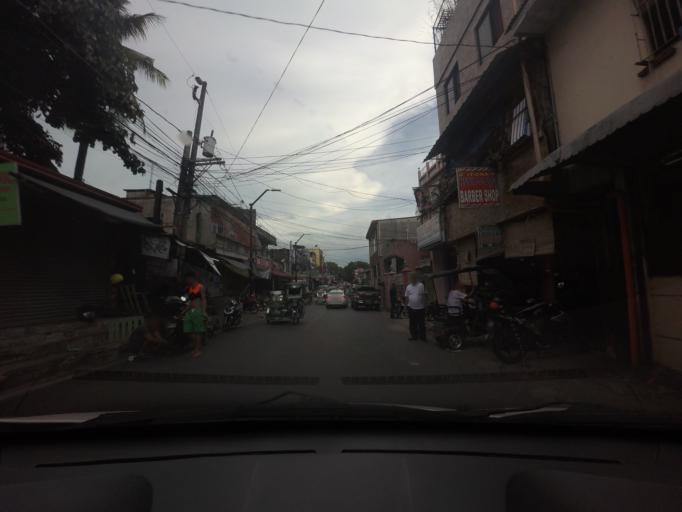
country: PH
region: Calabarzon
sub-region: Province of Rizal
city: Taguig
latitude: 14.5055
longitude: 121.0537
